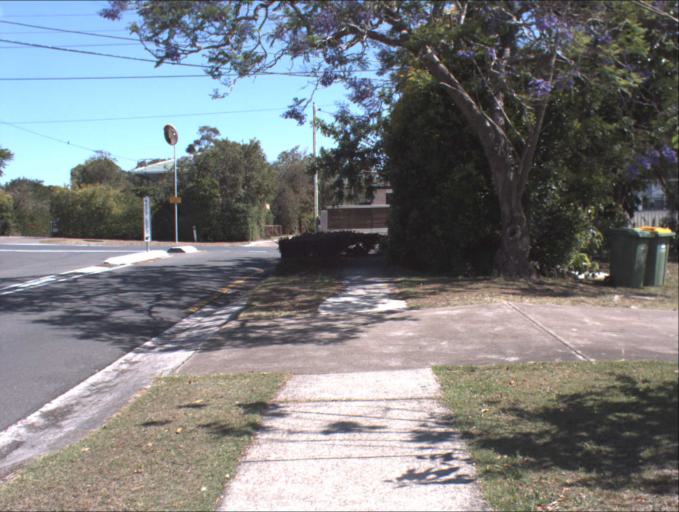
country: AU
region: Queensland
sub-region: Logan
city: Rochedale South
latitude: -27.5965
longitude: 153.1318
